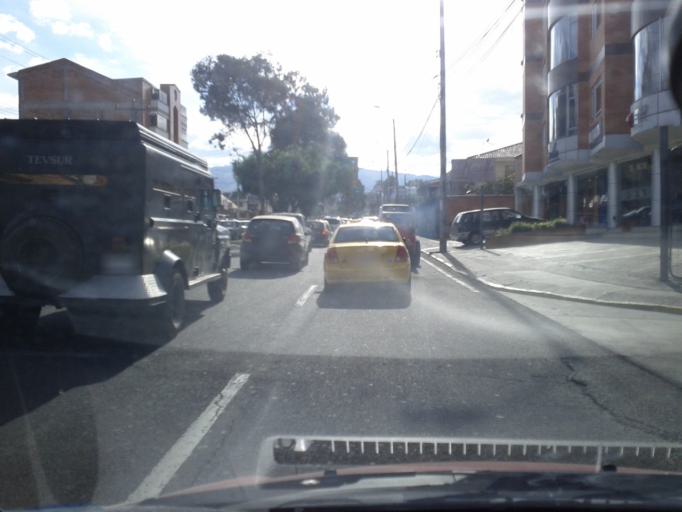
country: EC
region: Azuay
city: Cuenca
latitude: -2.8952
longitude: -79.0179
